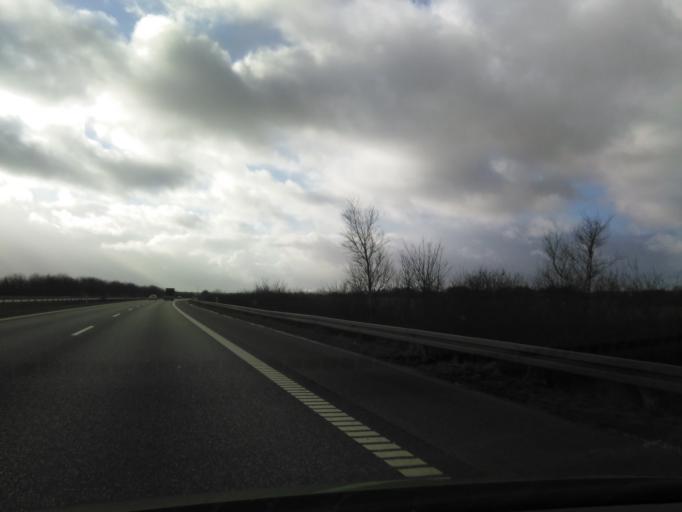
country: DK
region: Central Jutland
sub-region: Skanderborg Kommune
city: Stilling
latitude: 56.0807
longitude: 10.0091
